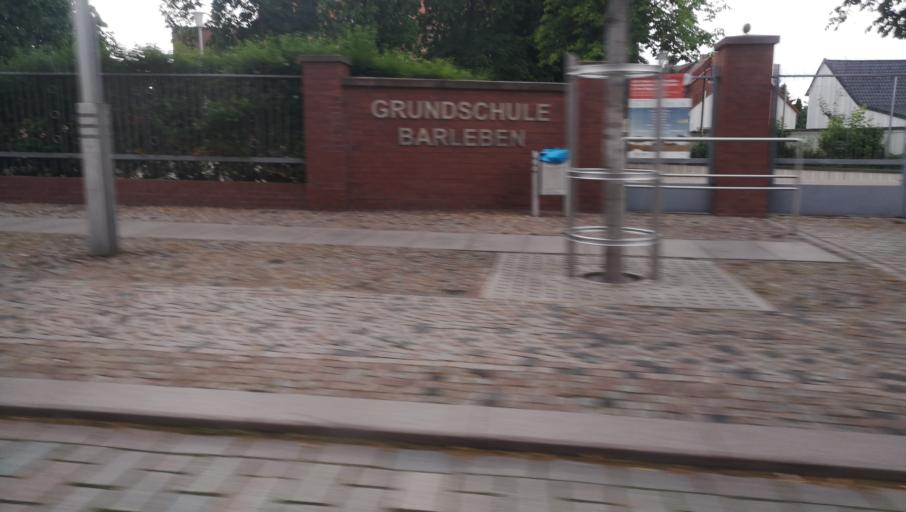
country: DE
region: Saxony-Anhalt
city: Barleben
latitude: 52.2053
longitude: 11.6187
